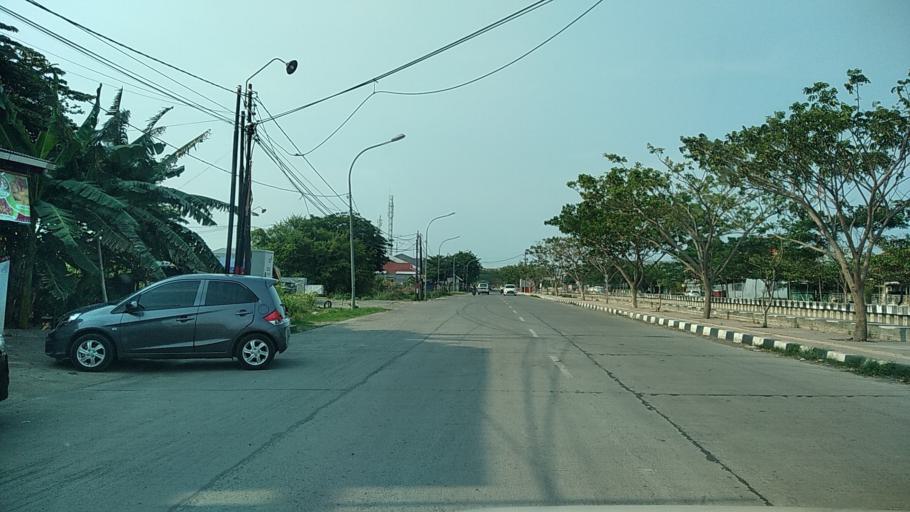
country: ID
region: Central Java
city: Semarang
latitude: -6.9587
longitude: 110.4101
